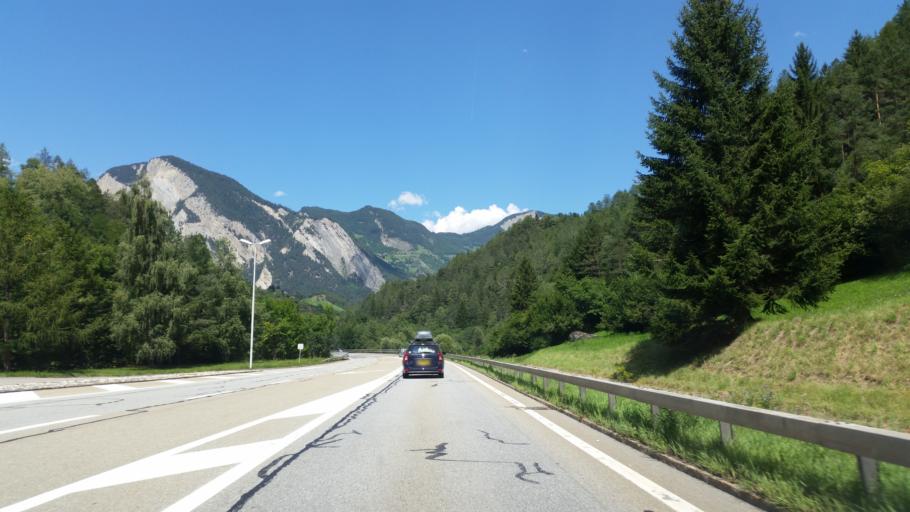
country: CH
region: Valais
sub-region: Entremont District
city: Orsieres
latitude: 46.0544
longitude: 7.1498
